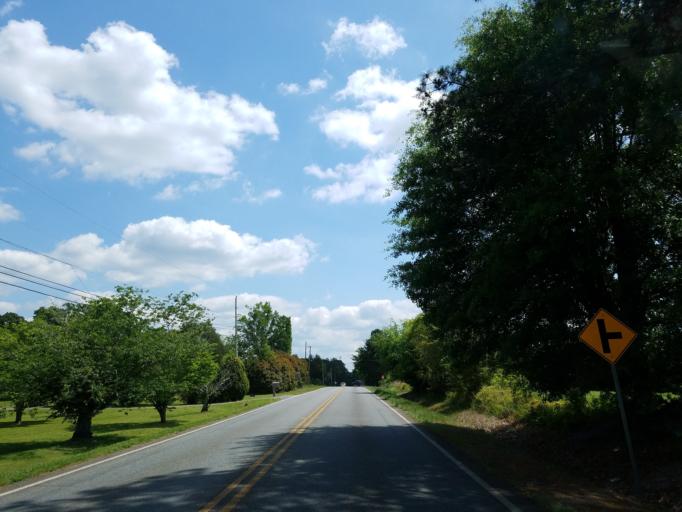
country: US
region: Georgia
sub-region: Monroe County
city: Forsyth
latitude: 33.0716
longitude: -83.9559
